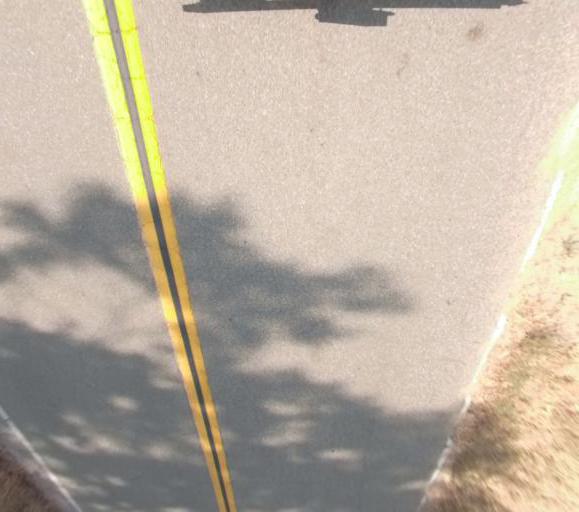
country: US
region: California
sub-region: Madera County
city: Oakhurst
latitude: 37.2376
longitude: -119.5277
